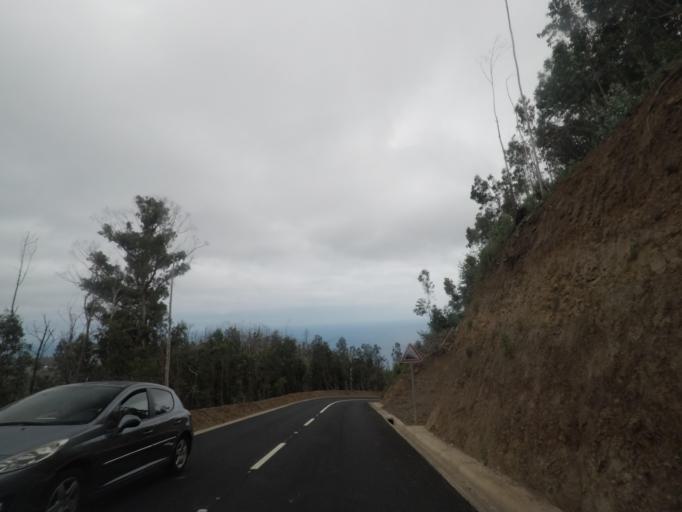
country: PT
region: Madeira
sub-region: Calheta
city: Estreito da Calheta
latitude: 32.7436
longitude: -17.1590
